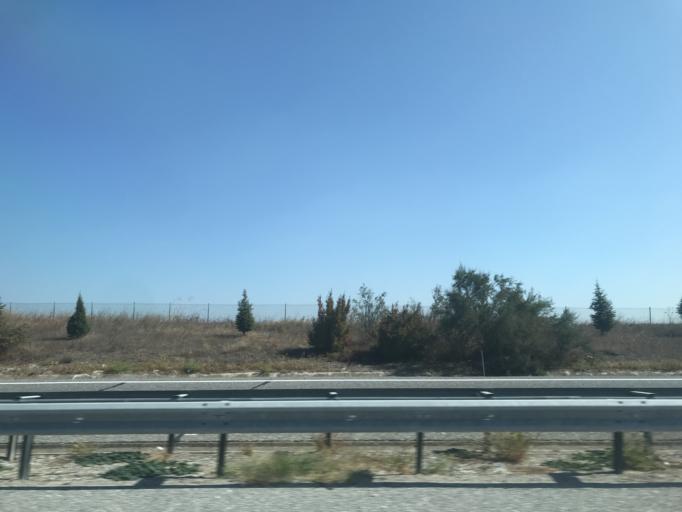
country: TR
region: Kirklareli
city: Luleburgaz
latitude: 41.3970
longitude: 27.3884
